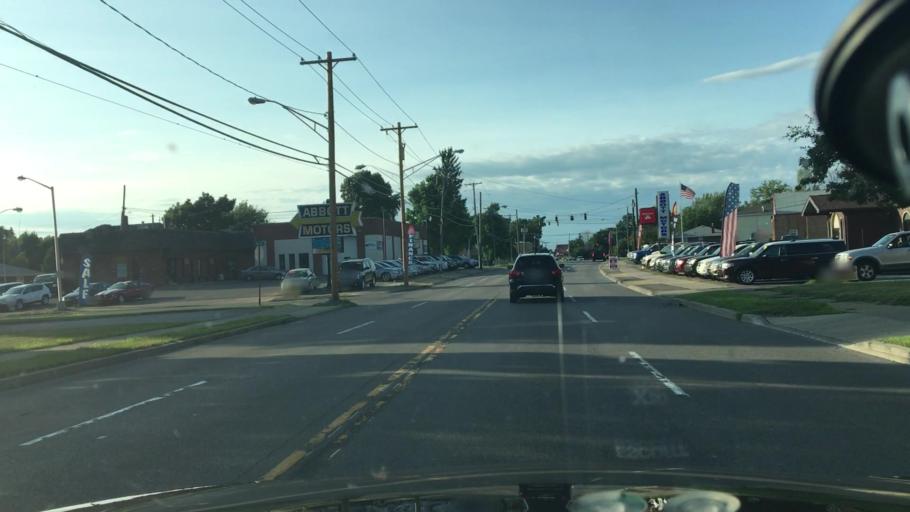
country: US
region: New York
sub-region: Erie County
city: Lackawanna
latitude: 42.8194
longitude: -78.8018
